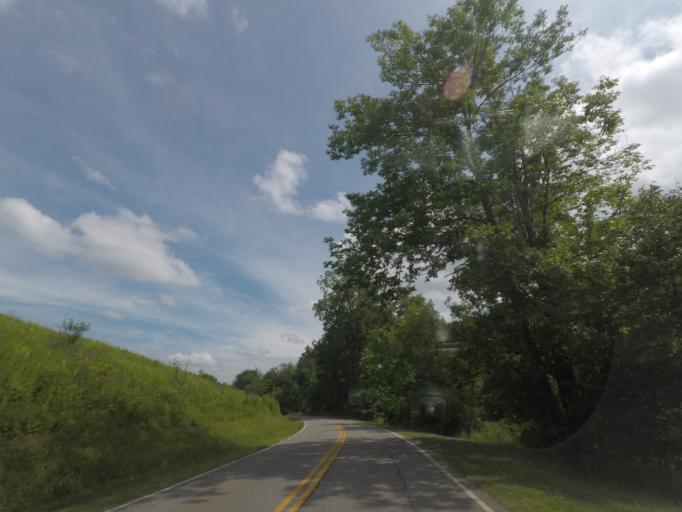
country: US
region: New York
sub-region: Saratoga County
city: Stillwater
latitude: 43.0018
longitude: -73.6116
